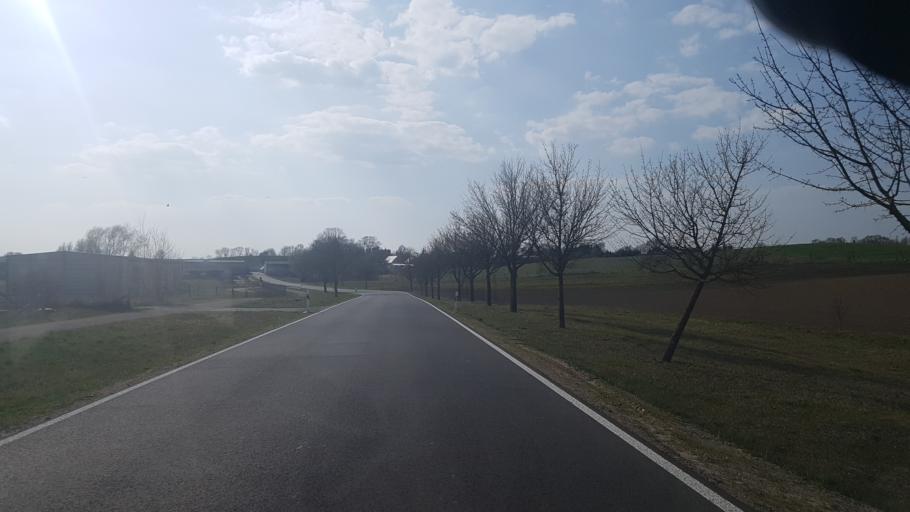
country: DE
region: Brandenburg
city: Gerswalde
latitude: 53.1747
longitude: 13.7828
